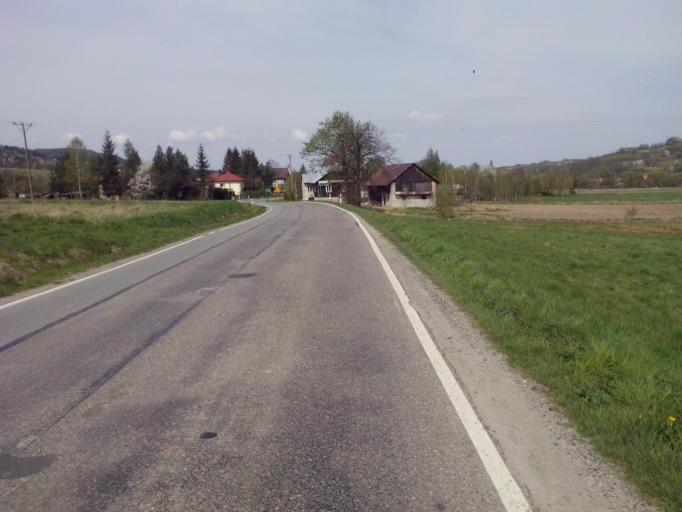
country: PL
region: Subcarpathian Voivodeship
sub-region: Powiat strzyzowski
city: Jawornik
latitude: 49.8044
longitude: 21.8595
